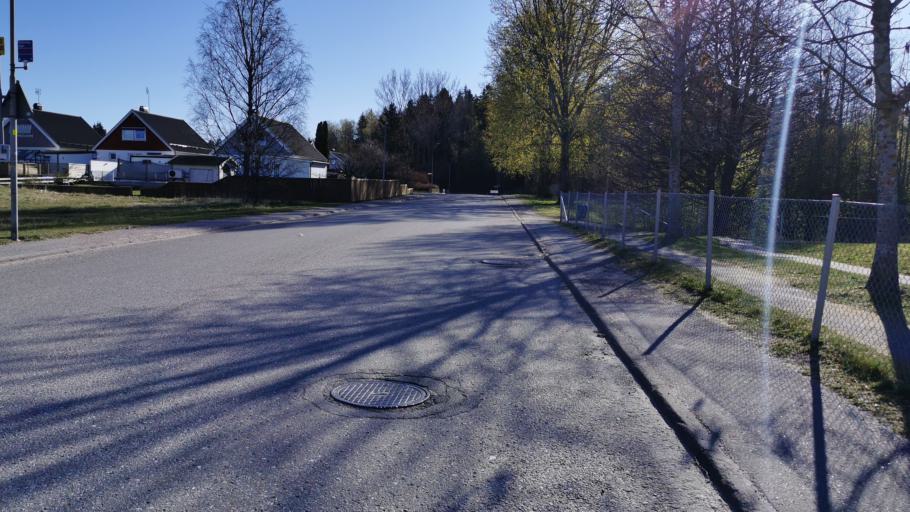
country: SE
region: OErebro
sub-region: Orebro Kommun
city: Hovsta
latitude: 59.3163
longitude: 15.2350
